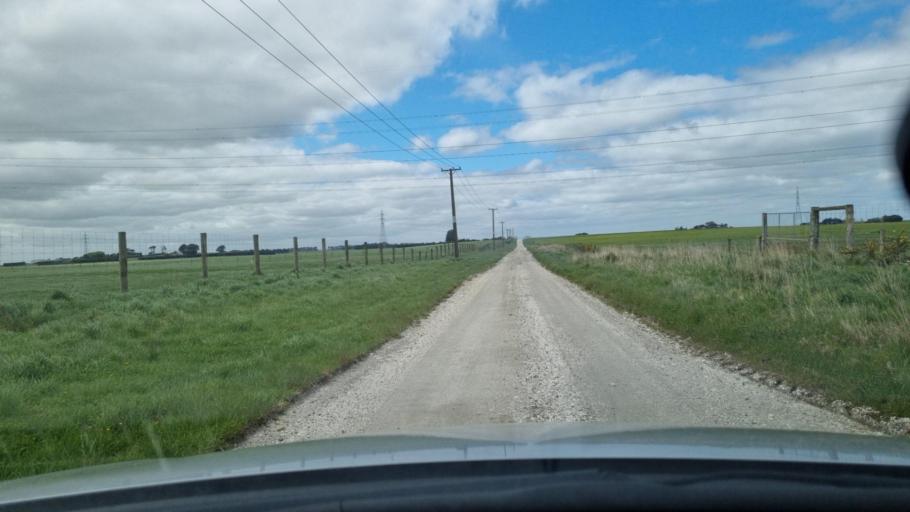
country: NZ
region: Southland
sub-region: Invercargill City
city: Invercargill
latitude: -46.4427
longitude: 168.4421
